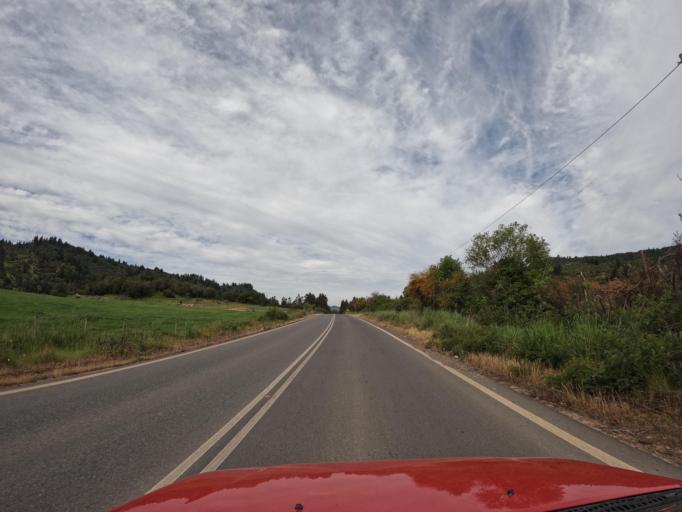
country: CL
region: Maule
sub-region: Provincia de Talca
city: Talca
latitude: -35.3229
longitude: -71.9490
